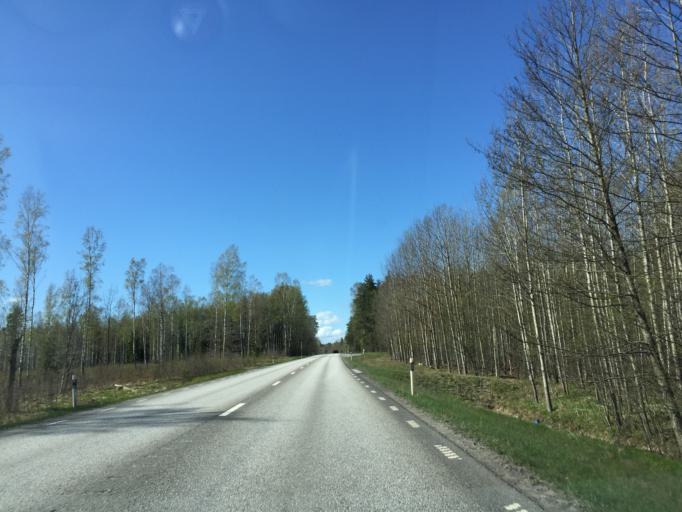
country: SE
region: OErebro
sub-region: Hallsbergs Kommun
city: Skollersta
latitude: 59.1327
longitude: 15.2899
